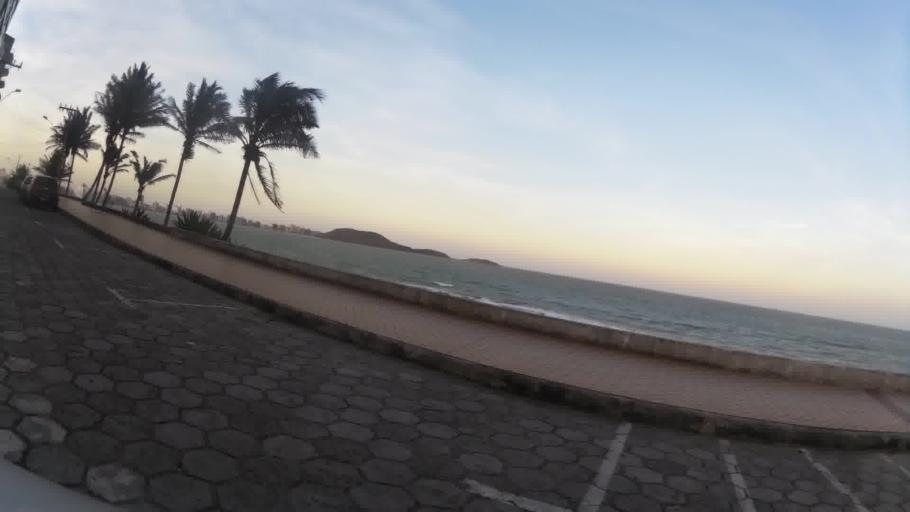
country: BR
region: Espirito Santo
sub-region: Guarapari
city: Guarapari
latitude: -20.6694
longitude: -40.4922
